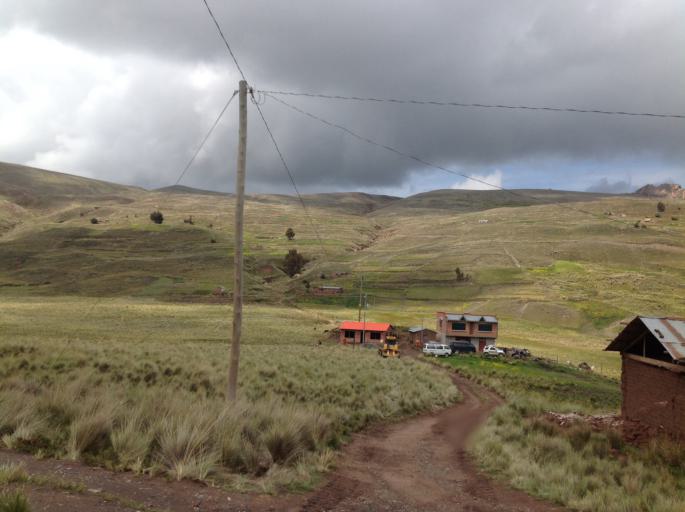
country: BO
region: La Paz
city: Yumani
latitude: -15.7688
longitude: -68.9845
